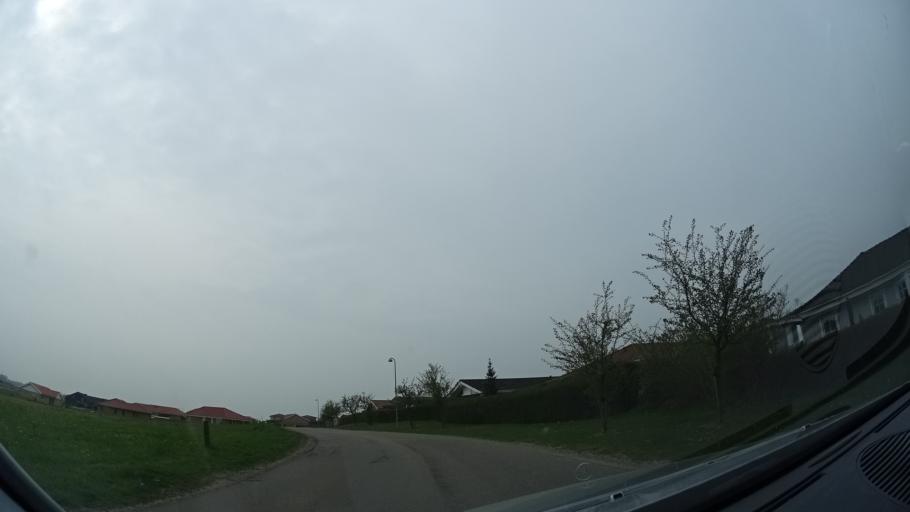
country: DK
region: Zealand
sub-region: Lejre Kommune
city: Ejby
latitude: 55.7016
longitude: 11.9010
